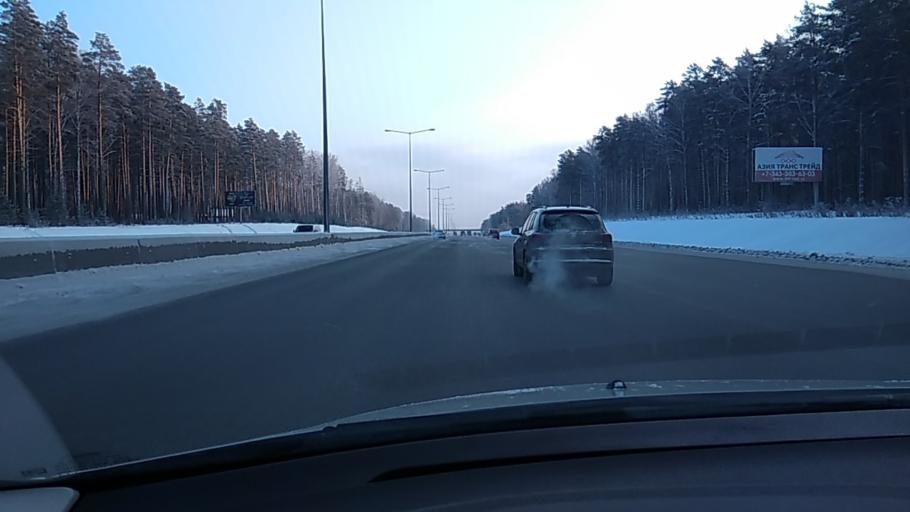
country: RU
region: Sverdlovsk
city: Istok
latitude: 56.7860
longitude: 60.6855
